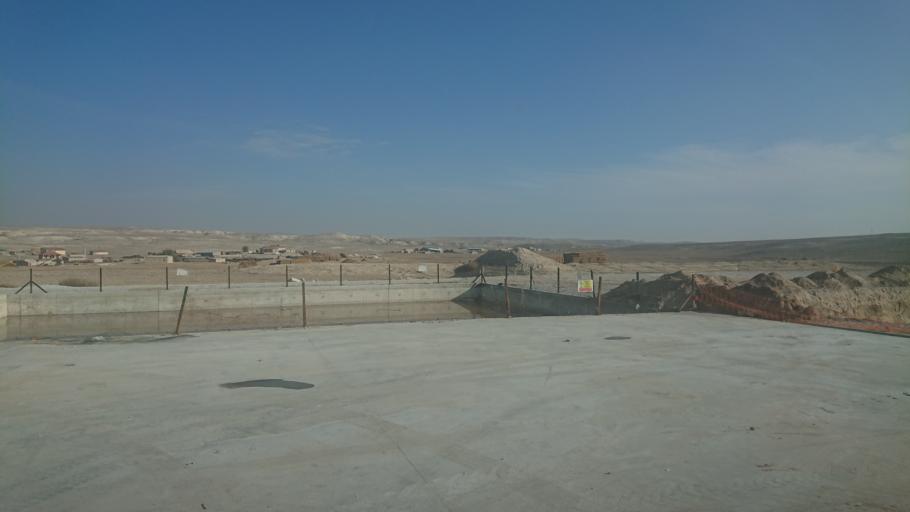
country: TR
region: Aksaray
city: Sultanhani
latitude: 38.0670
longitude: 33.6218
